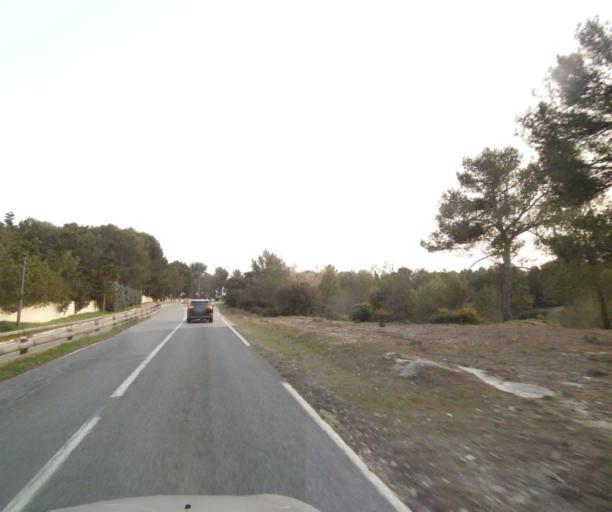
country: FR
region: Provence-Alpes-Cote d'Azur
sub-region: Departement des Bouches-du-Rhone
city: Cabries
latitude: 43.4484
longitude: 5.3608
